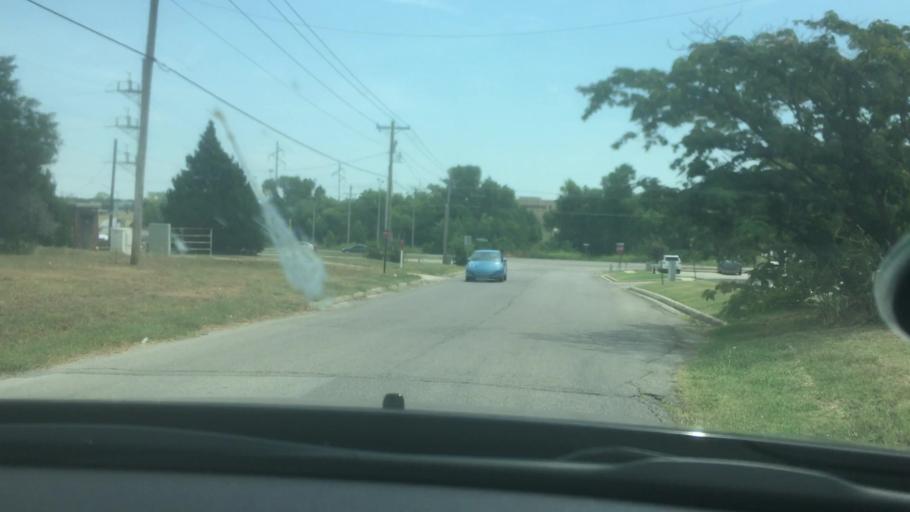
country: US
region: Oklahoma
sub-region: Carter County
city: Ardmore
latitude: 34.2020
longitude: -97.1446
